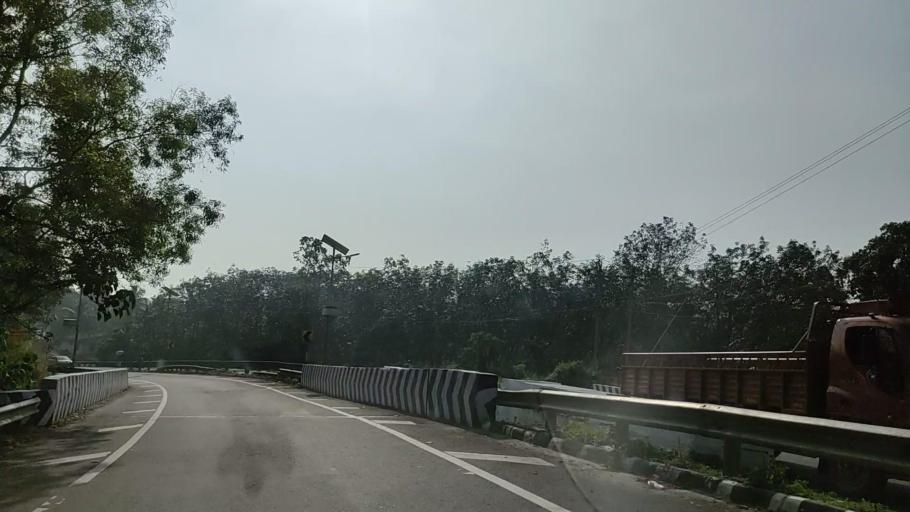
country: IN
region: Kerala
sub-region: Kollam
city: Punalur
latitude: 8.9765
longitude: 76.8148
